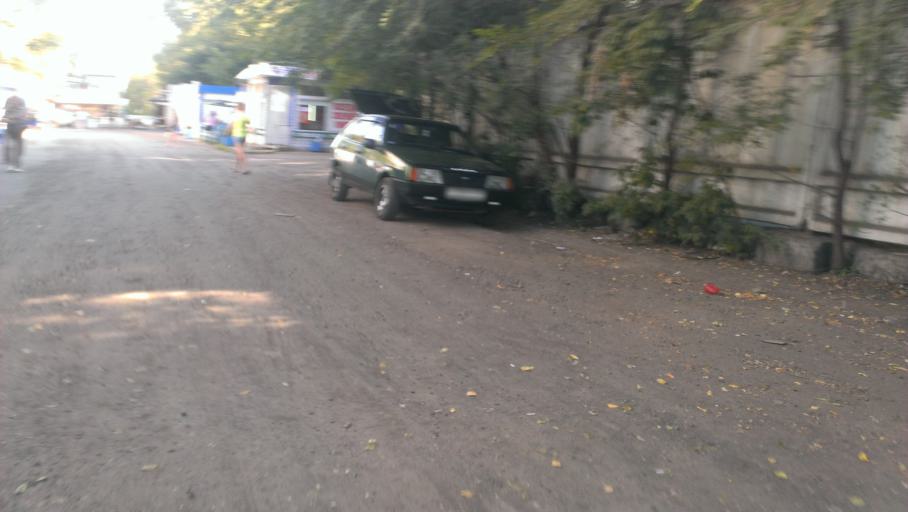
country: RU
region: Altai Krai
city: Novosilikatnyy
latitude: 53.3074
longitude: 83.6207
